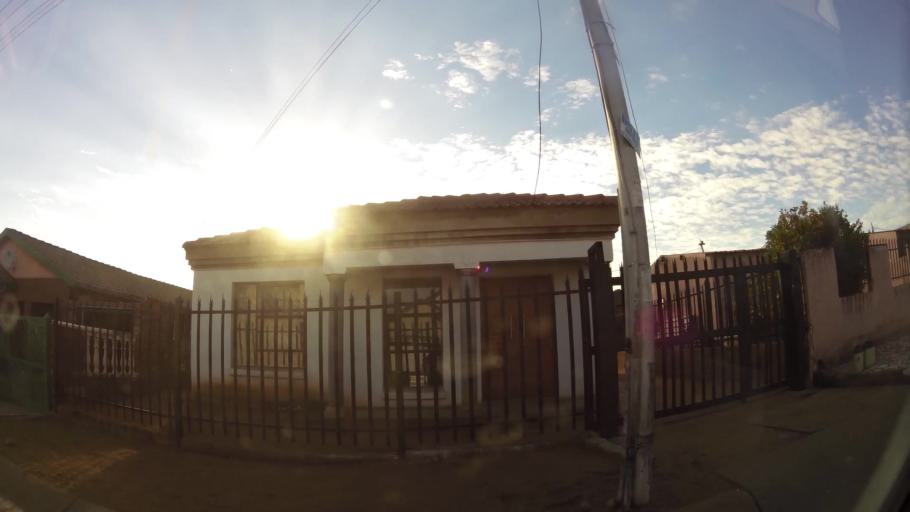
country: ZA
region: Gauteng
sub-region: City of Tshwane Metropolitan Municipality
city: Cullinan
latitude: -25.7059
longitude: 28.3879
